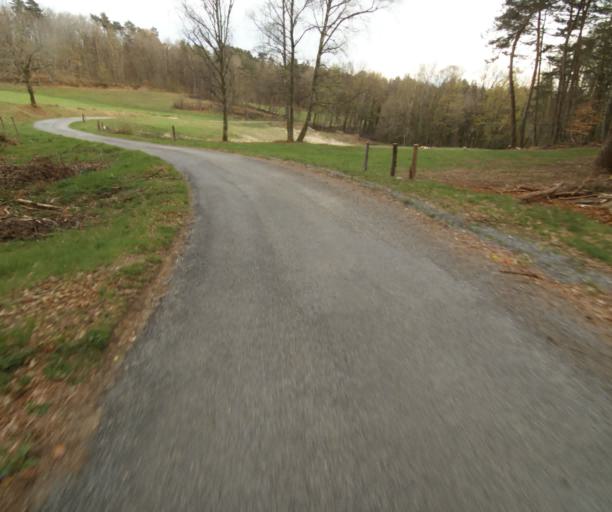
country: FR
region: Limousin
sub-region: Departement de la Correze
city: Argentat
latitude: 45.2017
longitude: 1.9873
